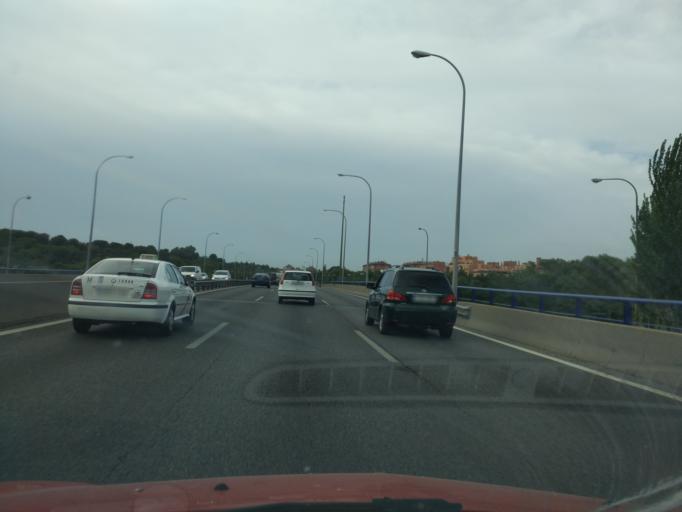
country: ES
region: Madrid
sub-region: Provincia de Madrid
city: Carabanchel
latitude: 40.3731
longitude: -3.7197
